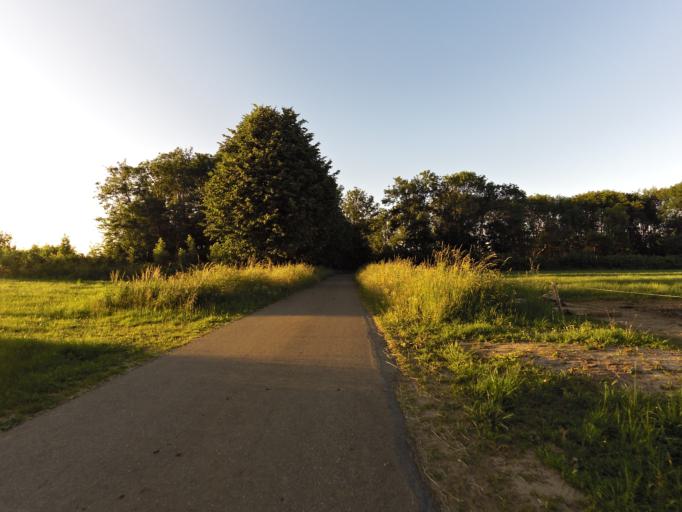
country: NL
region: Gelderland
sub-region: Gemeente Doesburg
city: Doesburg
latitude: 51.9954
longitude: 6.1696
